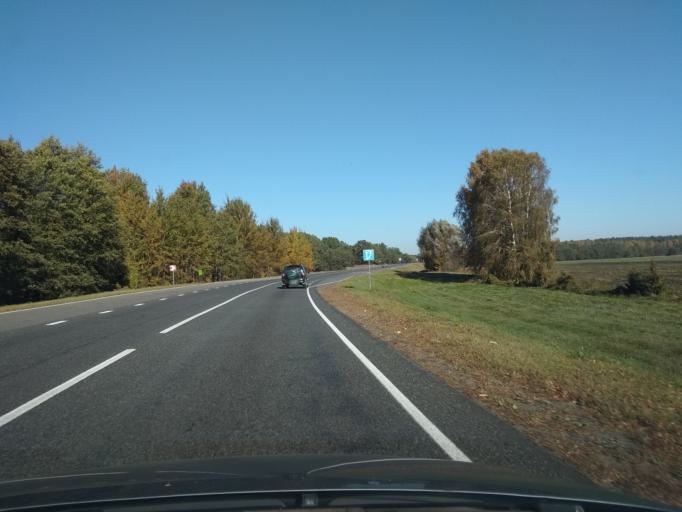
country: BY
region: Brest
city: Kobryn
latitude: 52.1294
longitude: 24.3051
